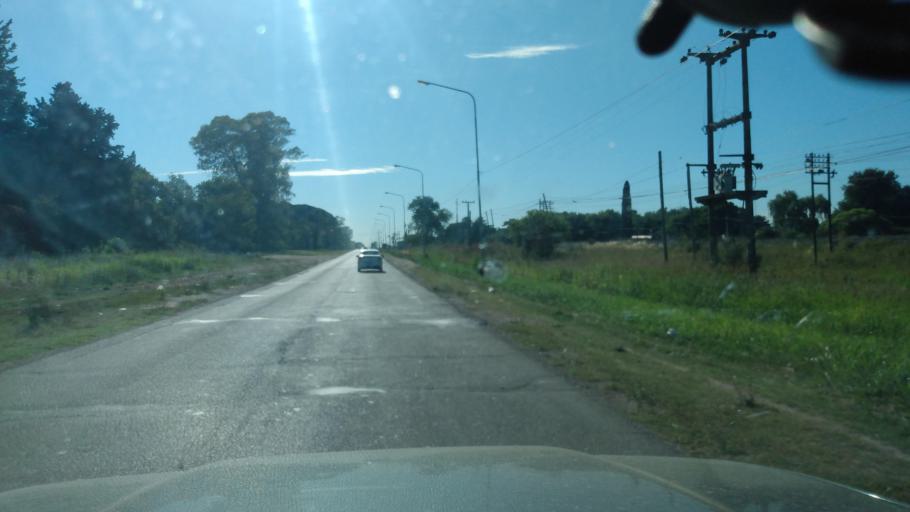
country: AR
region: Buenos Aires
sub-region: Partido de Lujan
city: Lujan
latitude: -34.5831
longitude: -59.0616
